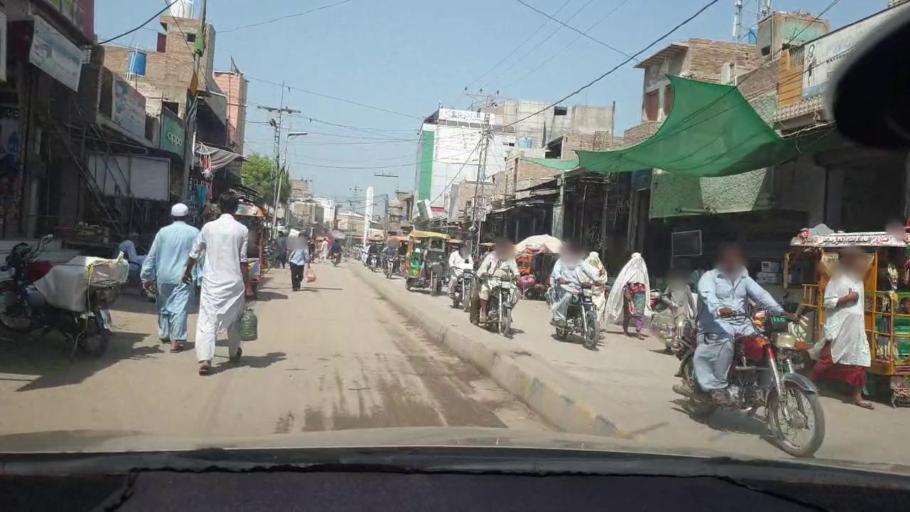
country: PK
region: Sindh
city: Kambar
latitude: 27.5898
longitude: 68.0036
